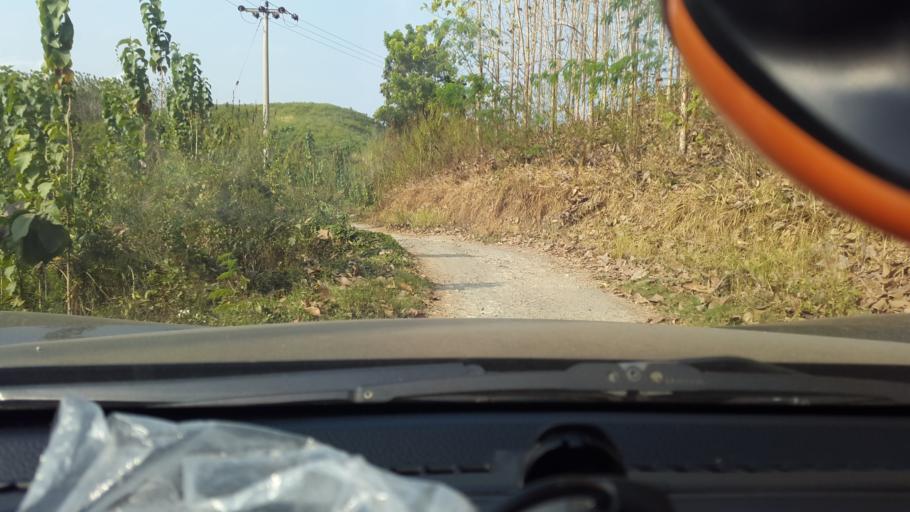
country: ID
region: West Java
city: Cikupa
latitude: -7.3593
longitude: 106.7007
